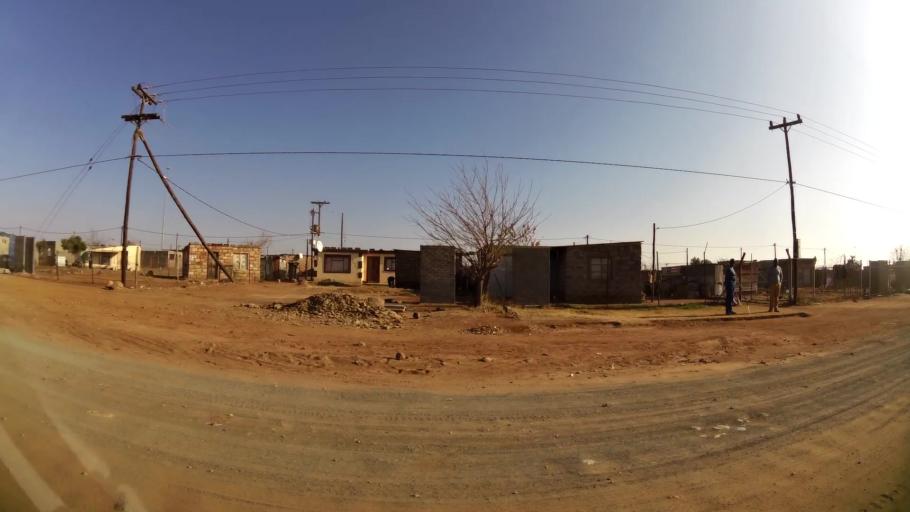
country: ZA
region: Orange Free State
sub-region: Mangaung Metropolitan Municipality
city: Bloemfontein
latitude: -29.2039
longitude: 26.2520
